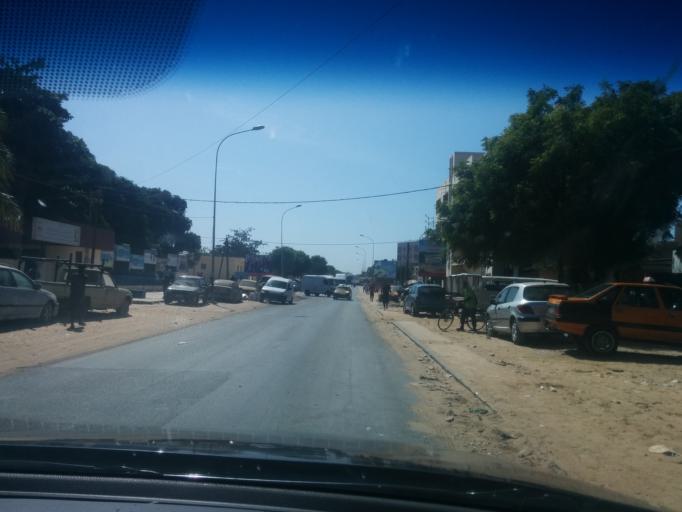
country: SN
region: Dakar
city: Grand Dakar
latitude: 14.7335
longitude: -17.4462
